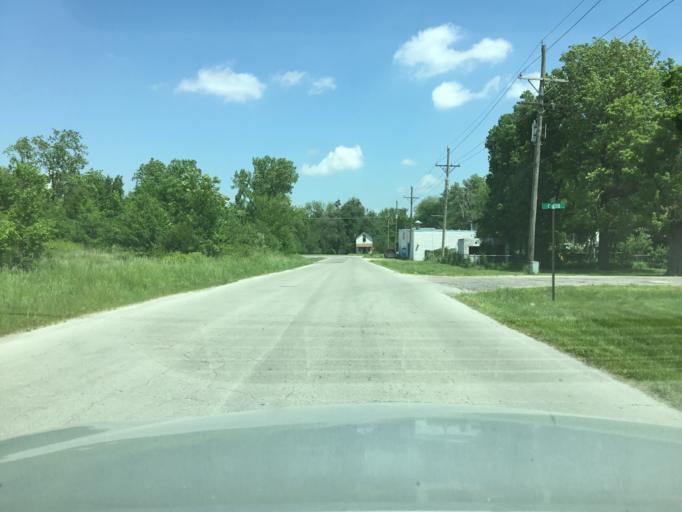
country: US
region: Kansas
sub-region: Labette County
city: Parsons
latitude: 37.3466
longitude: -95.2657
